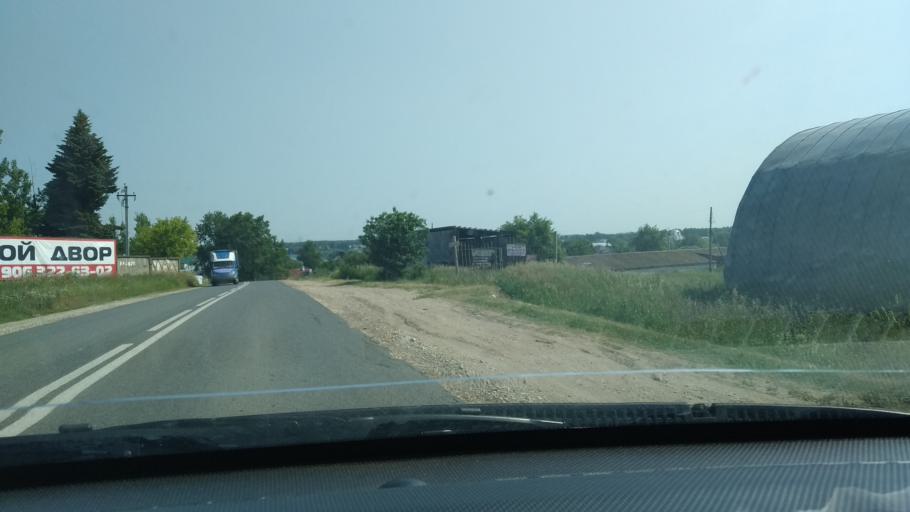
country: RU
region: Tatarstan
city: Osinovo
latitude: 55.9785
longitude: 48.7878
